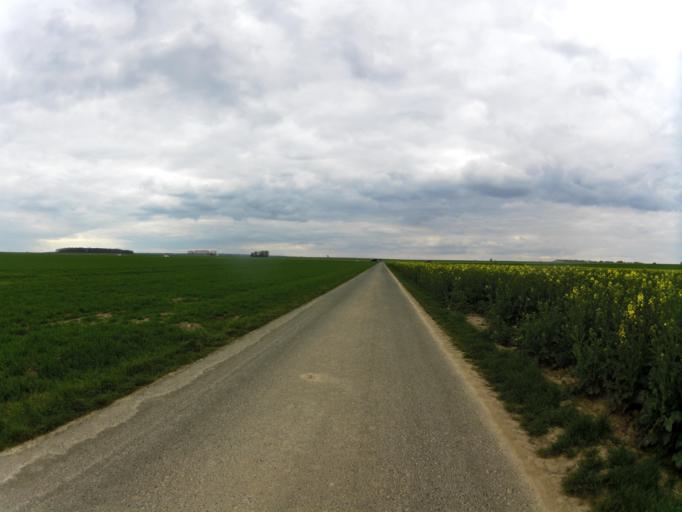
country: DE
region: Bavaria
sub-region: Regierungsbezirk Unterfranken
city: Giebelstadt
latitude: 49.6652
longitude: 9.9402
